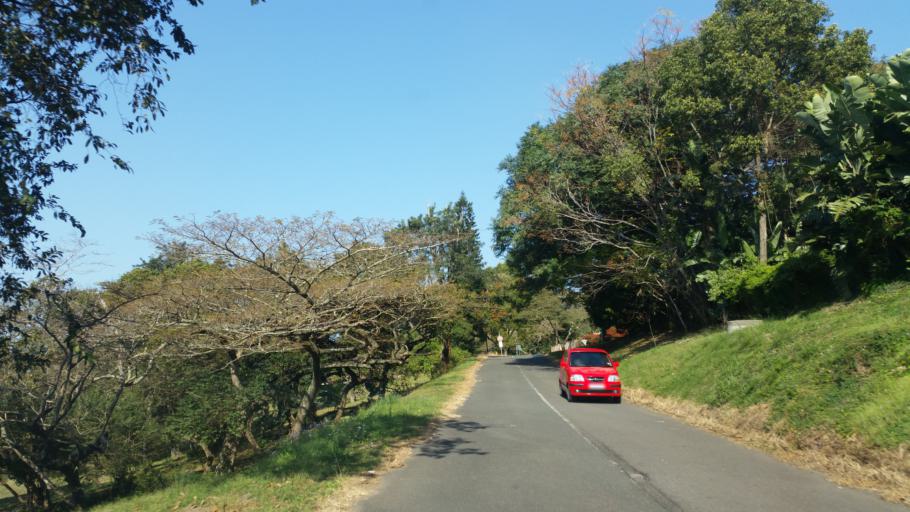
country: ZA
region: KwaZulu-Natal
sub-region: eThekwini Metropolitan Municipality
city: Berea
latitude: -29.8440
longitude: 30.9006
